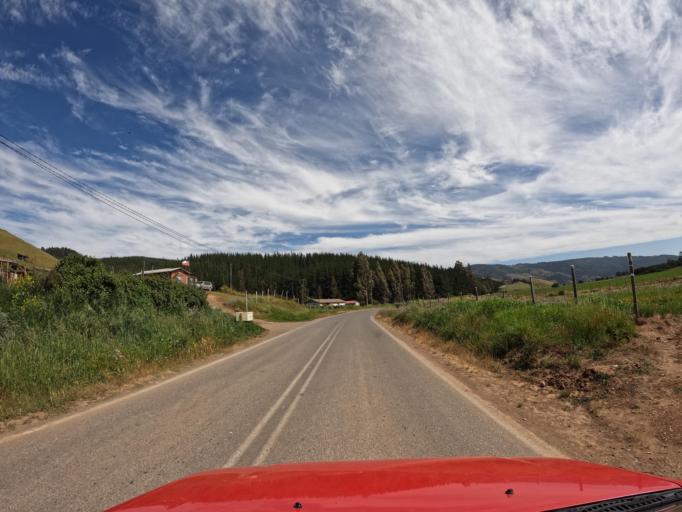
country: CL
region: Maule
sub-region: Provincia de Talca
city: Constitucion
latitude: -35.0339
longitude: -72.0534
